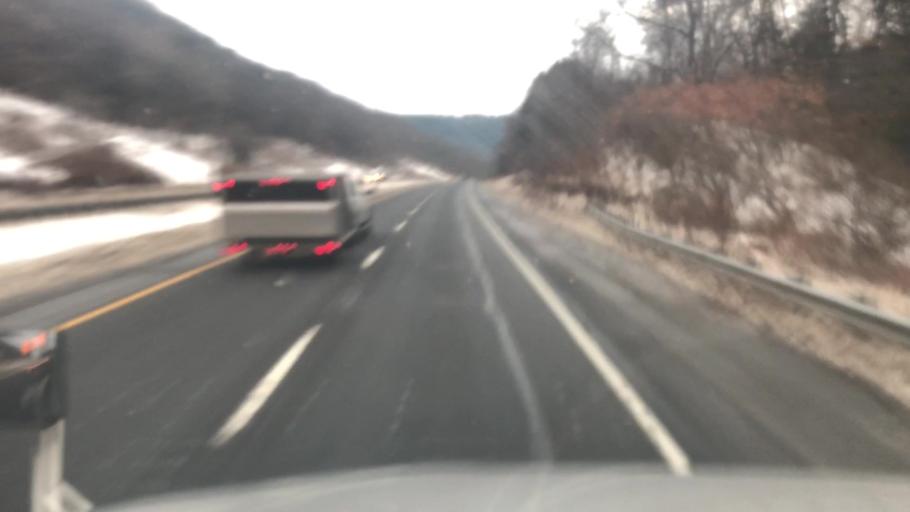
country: US
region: Pennsylvania
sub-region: Susquehanna County
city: Hallstead
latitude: 41.9347
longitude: -75.7318
